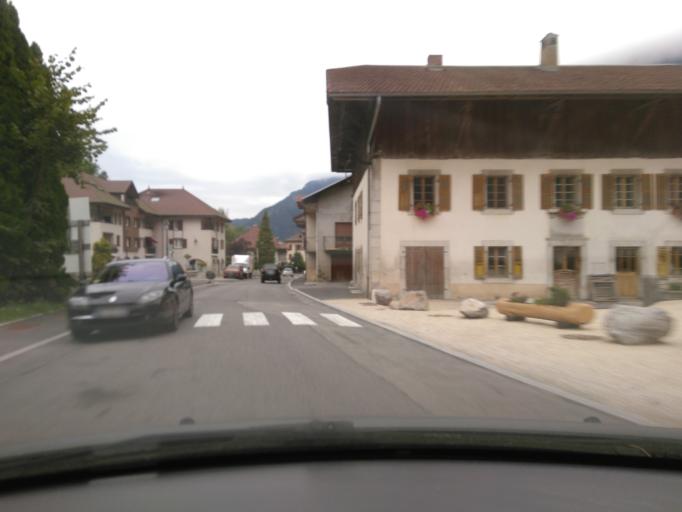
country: FR
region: Rhone-Alpes
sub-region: Departement de la Haute-Savoie
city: Le Grand-Bornand
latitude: 46.0009
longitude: 6.3961
